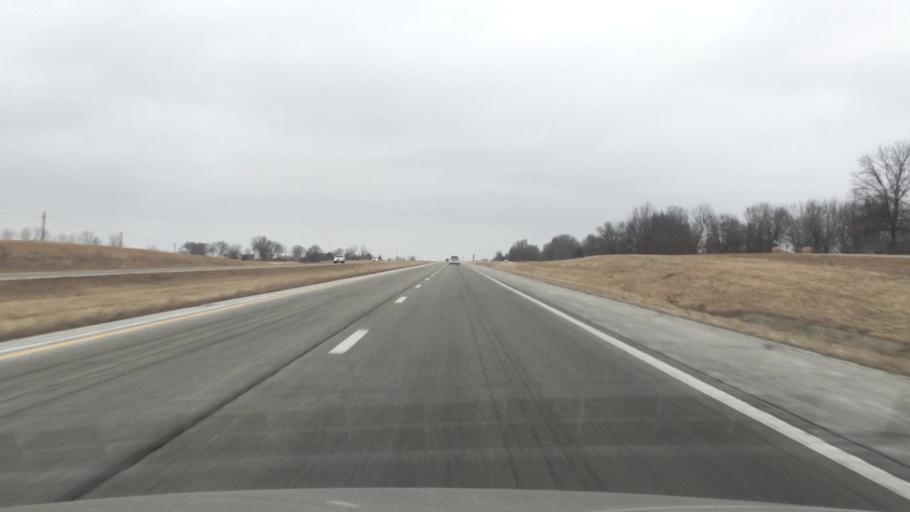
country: US
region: Missouri
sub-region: Cass County
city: Harrisonville
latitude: 38.5962
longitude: -94.3499
